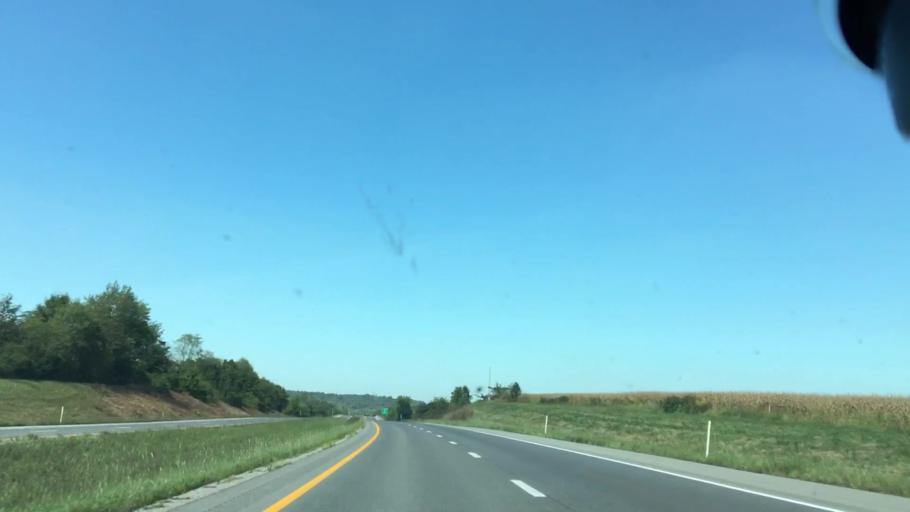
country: US
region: Kentucky
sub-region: Webster County
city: Sebree
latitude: 37.5747
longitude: -87.4801
